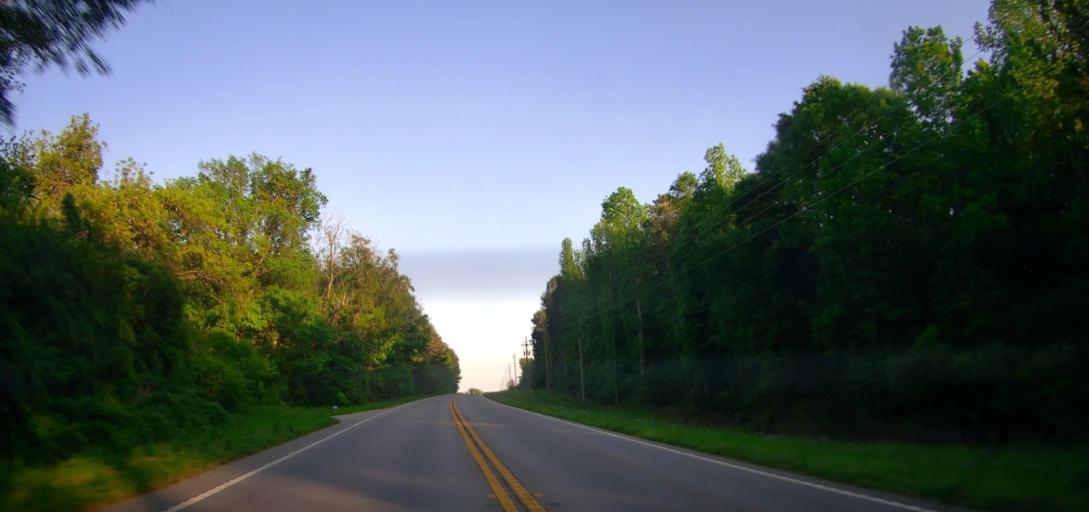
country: US
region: Georgia
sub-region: Walton County
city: Social Circle
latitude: 33.5645
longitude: -83.7553
